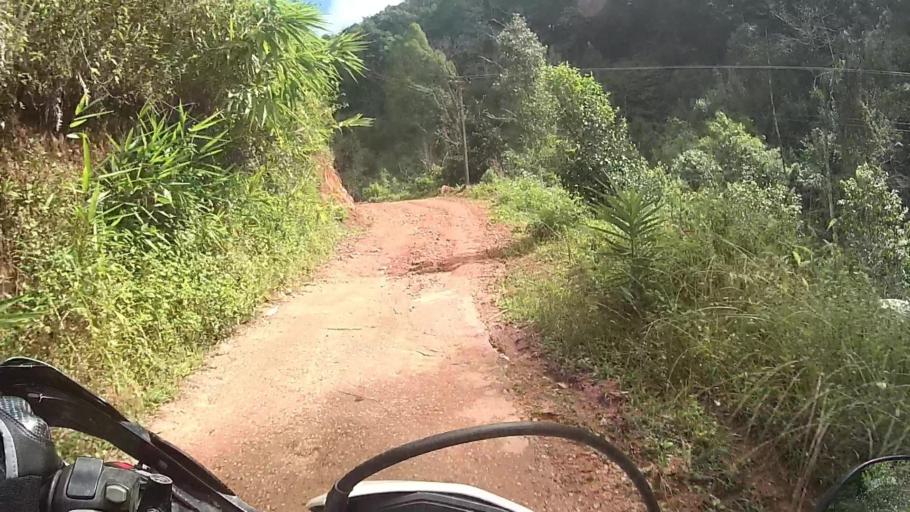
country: TH
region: Lampang
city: Mueang Pan
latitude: 18.9775
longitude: 99.4317
